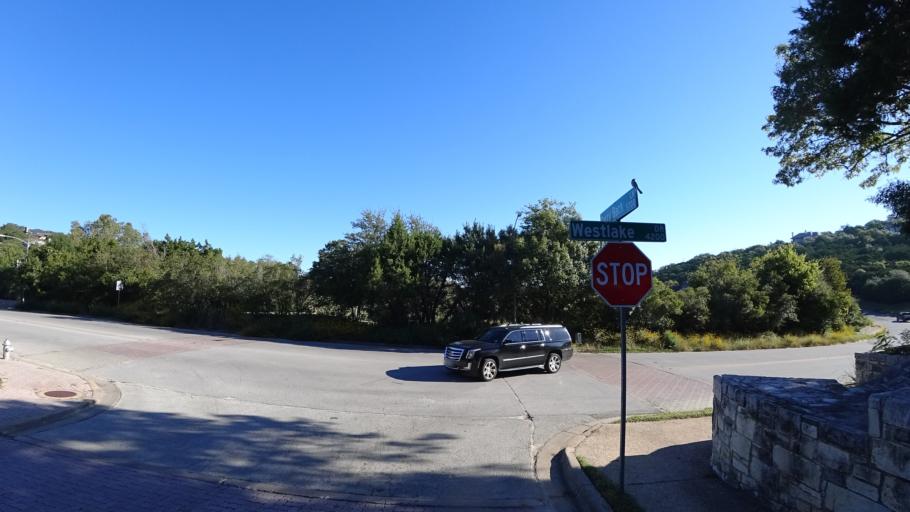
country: US
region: Texas
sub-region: Travis County
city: West Lake Hills
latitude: 30.3328
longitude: -97.8009
